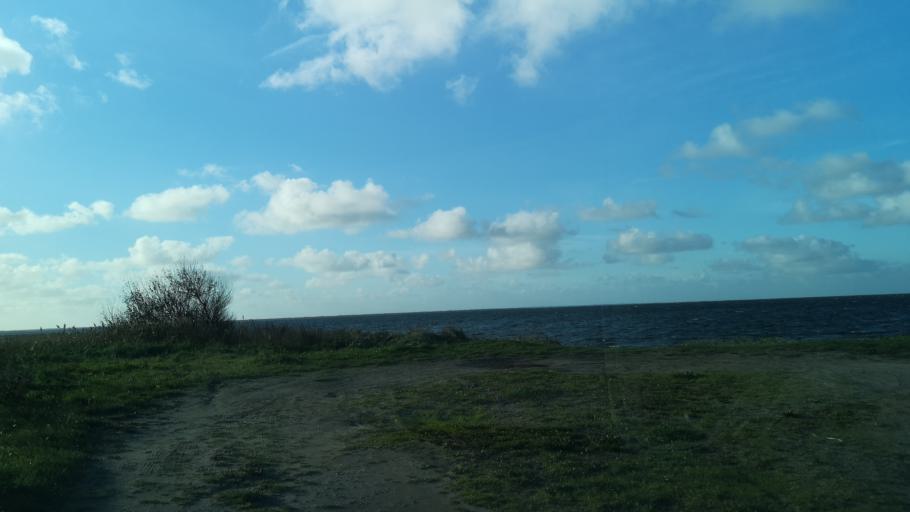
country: DK
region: Central Jutland
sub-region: Ringkobing-Skjern Kommune
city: Skjern
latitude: 55.8684
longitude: 8.3260
